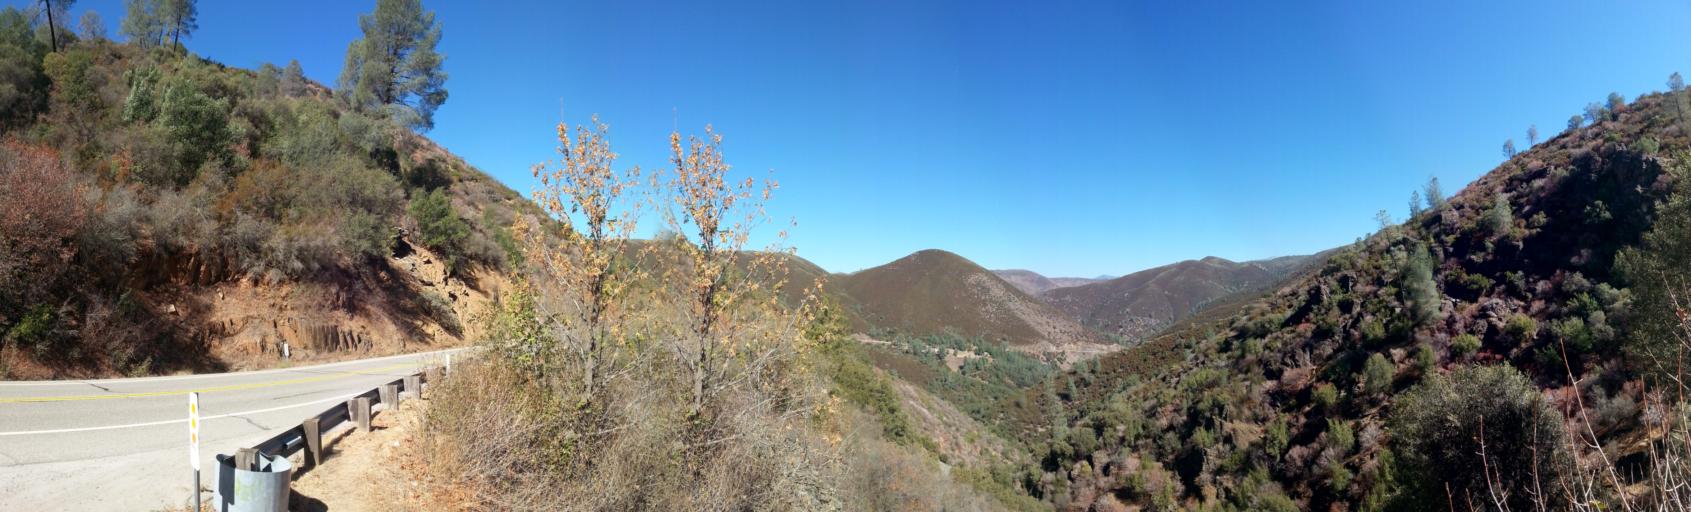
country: US
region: California
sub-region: Mariposa County
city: Yosemite Valley
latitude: 37.6937
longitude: -119.7270
